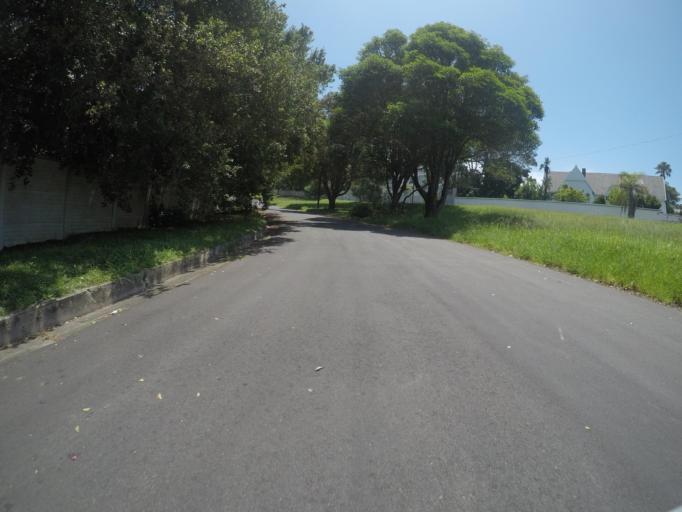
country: ZA
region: Eastern Cape
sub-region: Buffalo City Metropolitan Municipality
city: East London
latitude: -33.0001
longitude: 27.9274
